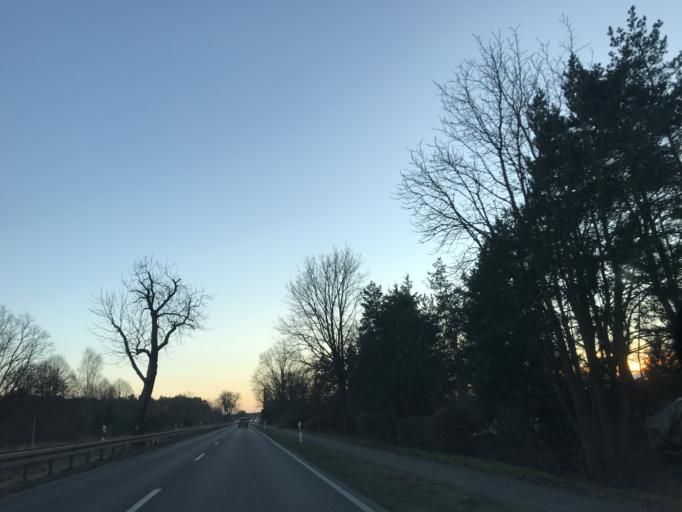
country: DE
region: Brandenburg
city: Rathenow
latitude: 52.5689
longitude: 12.3326
